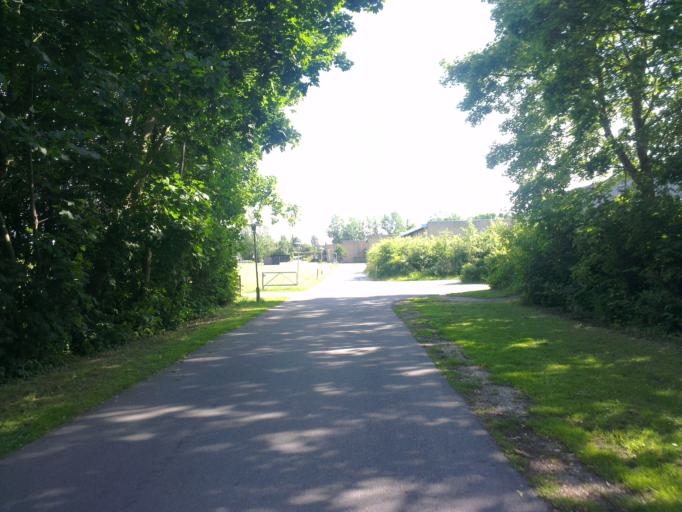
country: DK
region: Capital Region
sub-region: Frederikssund Kommune
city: Skibby
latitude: 55.7477
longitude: 11.9663
